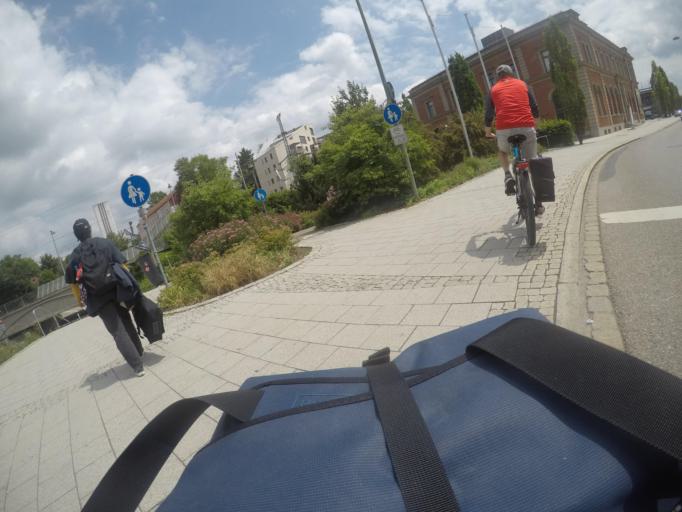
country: DE
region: Bavaria
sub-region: Swabia
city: Memmingen
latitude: 47.9869
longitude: 10.1864
